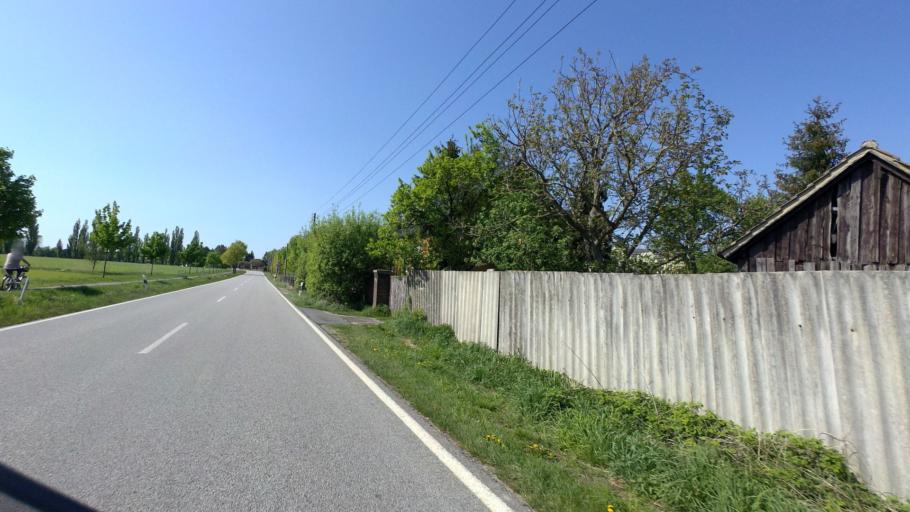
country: DE
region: Brandenburg
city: Schlepzig
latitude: 52.0478
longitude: 14.0156
